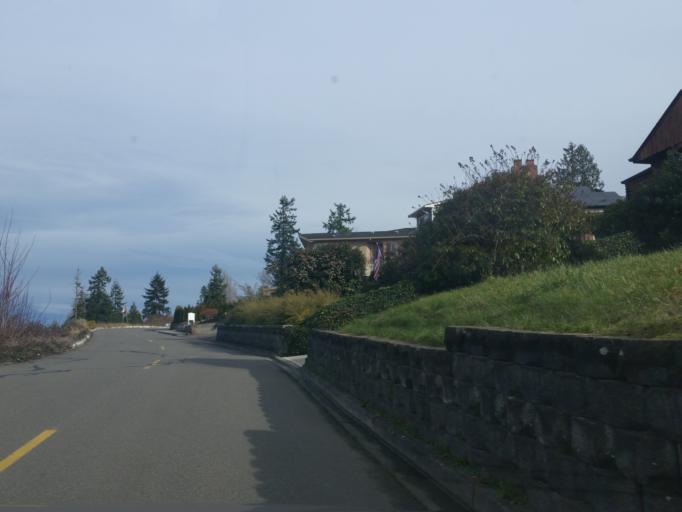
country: US
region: Washington
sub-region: Snohomish County
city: Mukilteo
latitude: 47.9511
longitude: -122.2903
